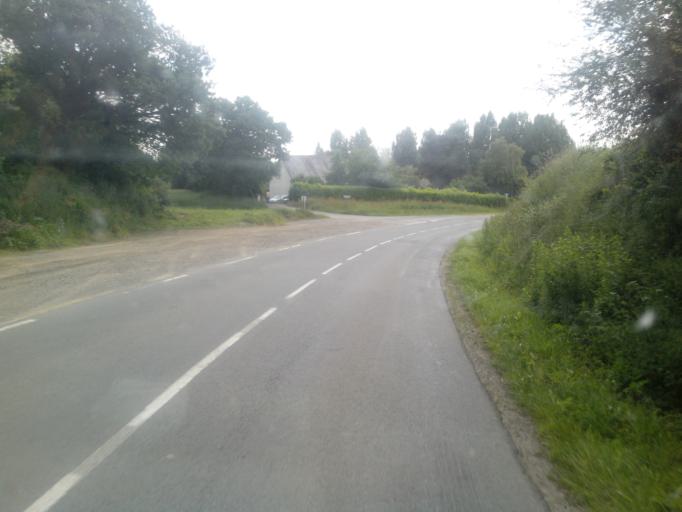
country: FR
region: Brittany
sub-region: Departement d'Ille-et-Vilaine
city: Montreuil-sur-Ille
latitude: 48.3208
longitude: -1.6466
